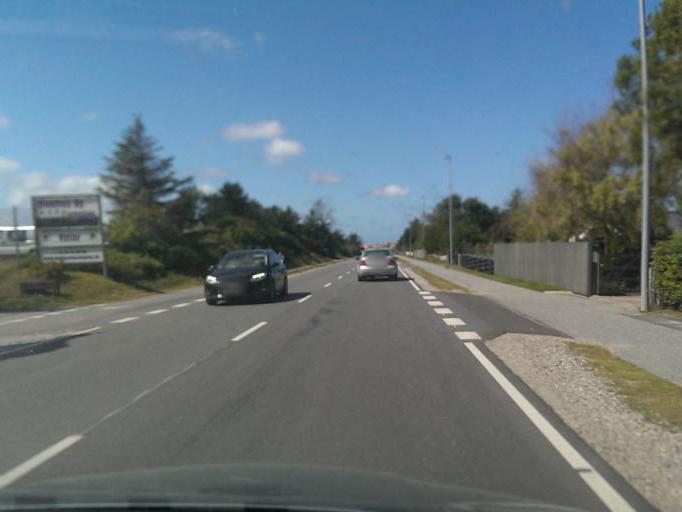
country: DK
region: North Denmark
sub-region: Jammerbugt Kommune
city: Pandrup
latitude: 57.2503
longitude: 9.5983
